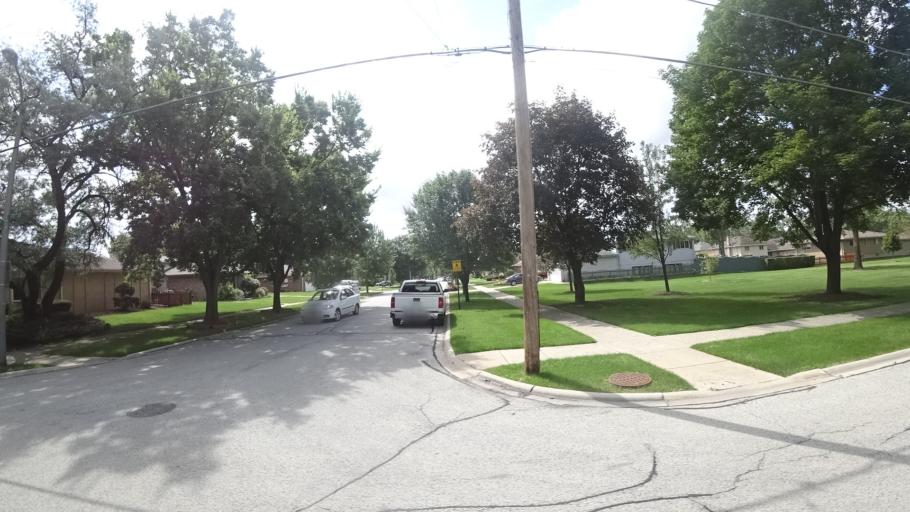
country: US
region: Illinois
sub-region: Cook County
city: Tinley Park
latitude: 41.5697
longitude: -87.7781
